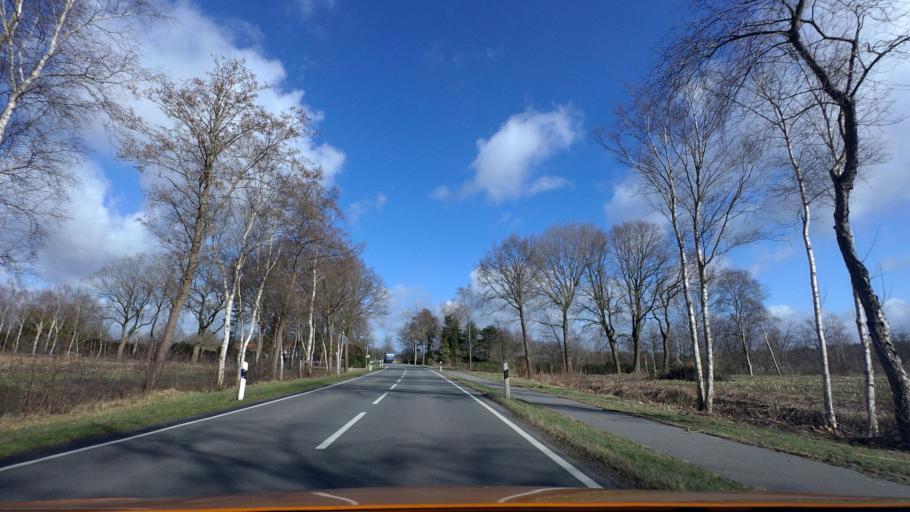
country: DE
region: Lower Saxony
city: Edewecht
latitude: 53.0992
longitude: 7.9502
